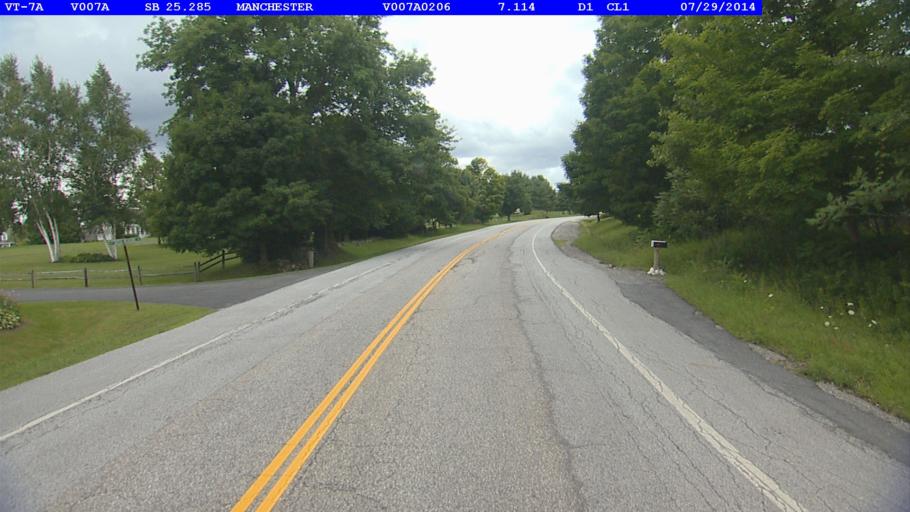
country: US
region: Vermont
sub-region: Bennington County
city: Manchester Center
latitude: 43.1990
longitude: -73.0292
